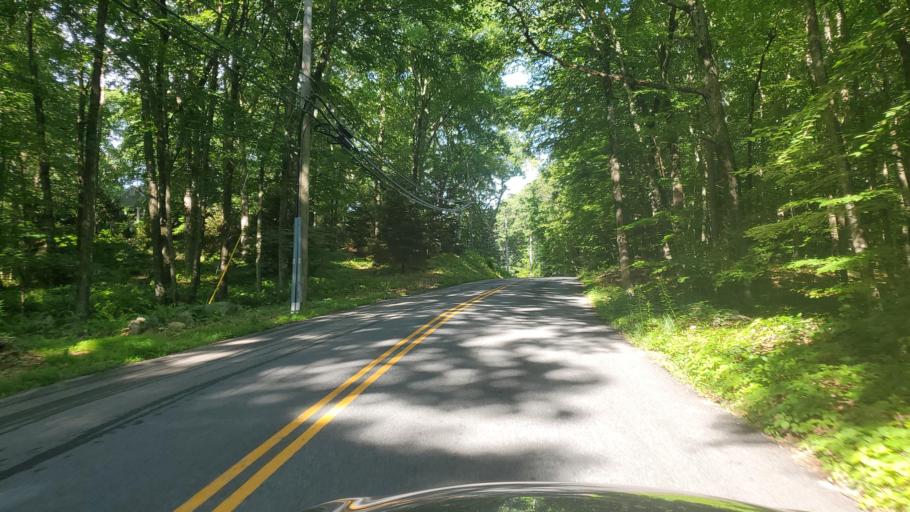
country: US
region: Connecticut
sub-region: Fairfield County
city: Newtown
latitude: 41.3775
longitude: -73.3135
